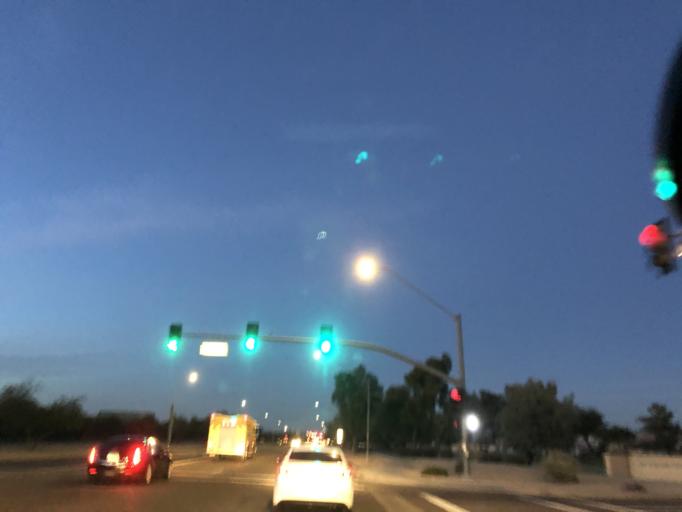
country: US
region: Arizona
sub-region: Maricopa County
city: Glendale
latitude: 33.5745
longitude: -112.1861
